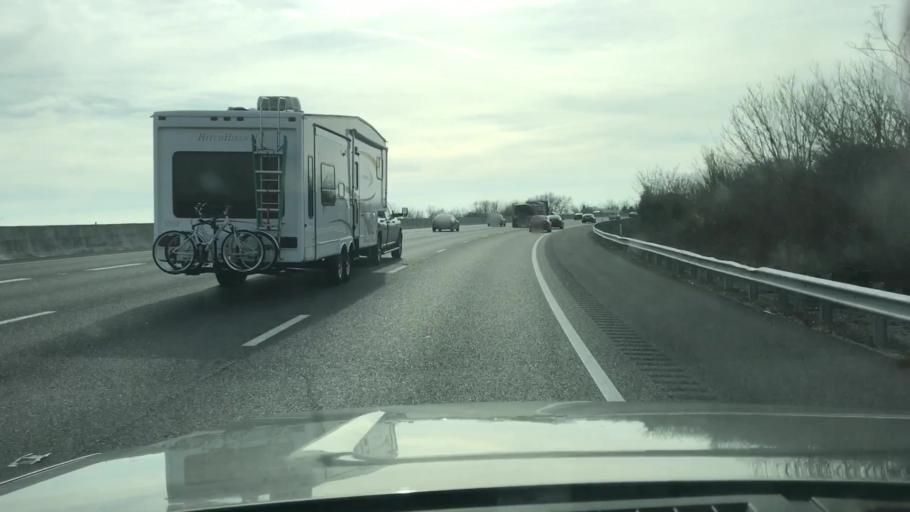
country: US
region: Tennessee
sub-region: Williamson County
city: Brentwood Estates
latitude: 36.0117
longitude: -86.7854
